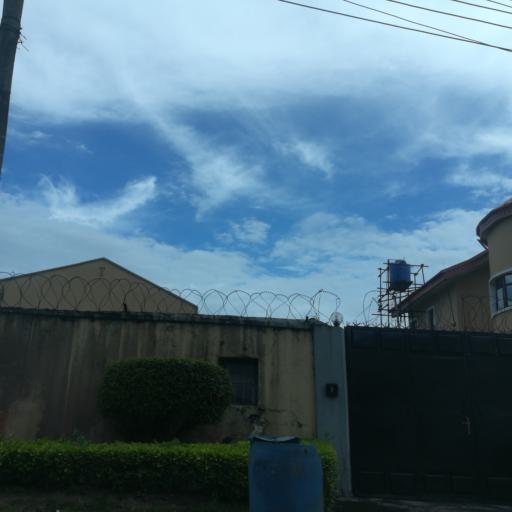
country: NG
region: Lagos
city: Ikoyi
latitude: 6.4458
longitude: 3.4729
